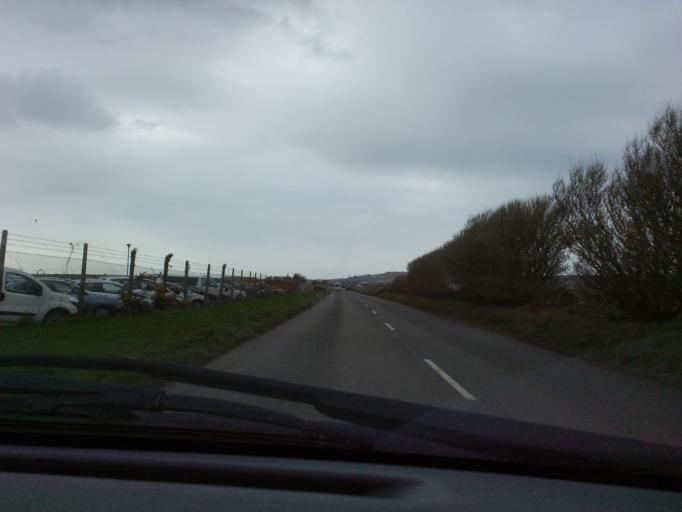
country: GB
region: England
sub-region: Cornwall
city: Saint Just
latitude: 50.1027
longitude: -5.6681
